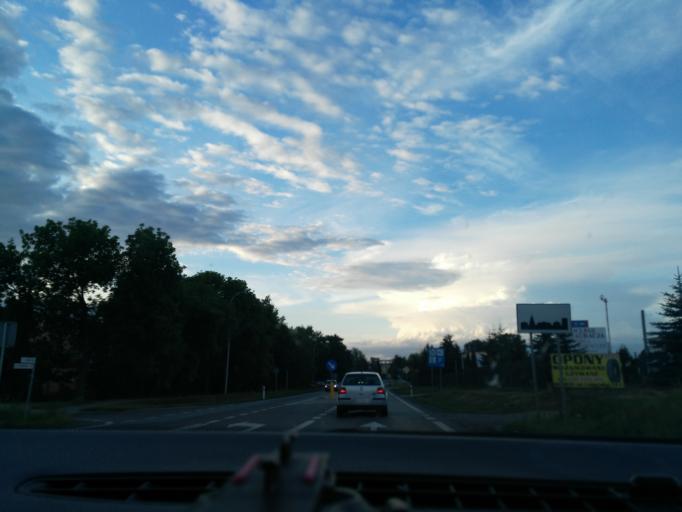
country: PL
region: Lublin Voivodeship
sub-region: Powiat lubelski
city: Niemce
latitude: 51.3543
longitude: 22.6207
